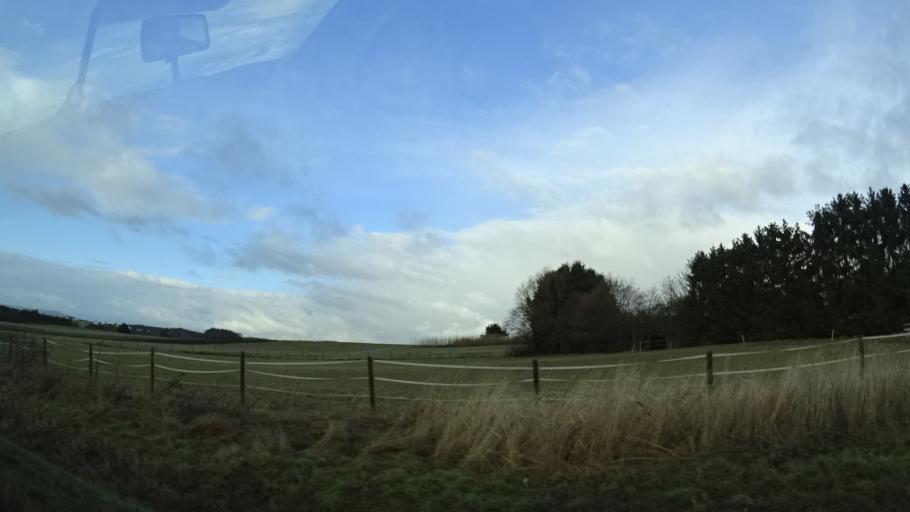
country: DE
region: Hesse
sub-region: Regierungsbezirk Giessen
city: Lich
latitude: 50.5465
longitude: 8.7644
